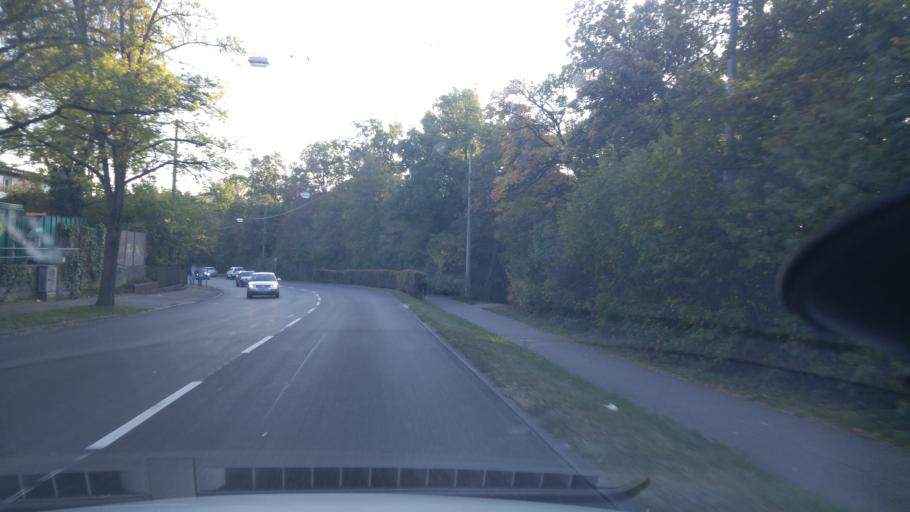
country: DE
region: Baden-Wuerttemberg
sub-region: Regierungsbezirk Stuttgart
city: Stuttgart Feuerbach
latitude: 48.7782
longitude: 9.1375
